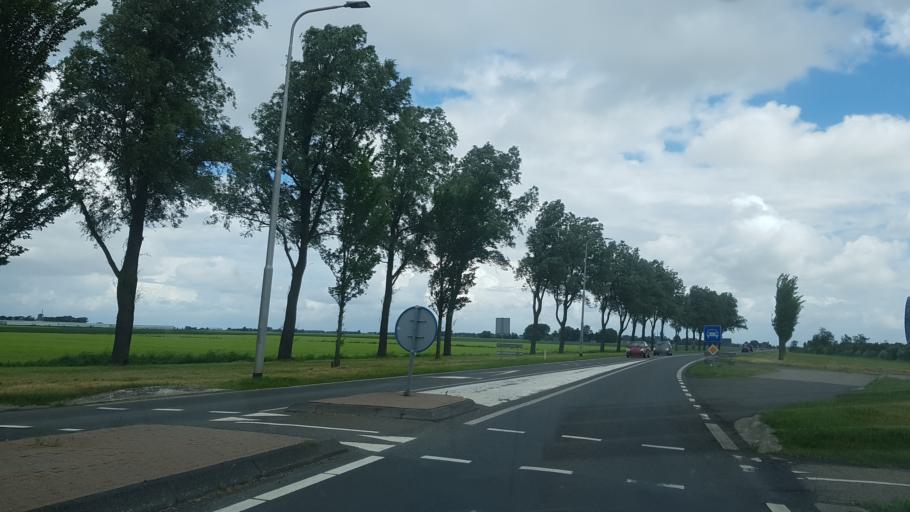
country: NL
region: Friesland
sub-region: Gemeente Dongeradeel
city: Anjum
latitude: 53.3583
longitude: 6.0756
